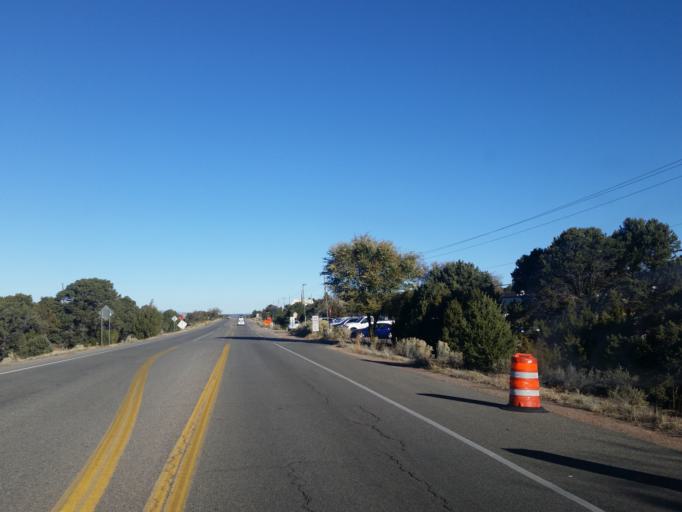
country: US
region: New Mexico
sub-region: Santa Fe County
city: Santa Fe
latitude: 35.6260
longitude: -105.9207
